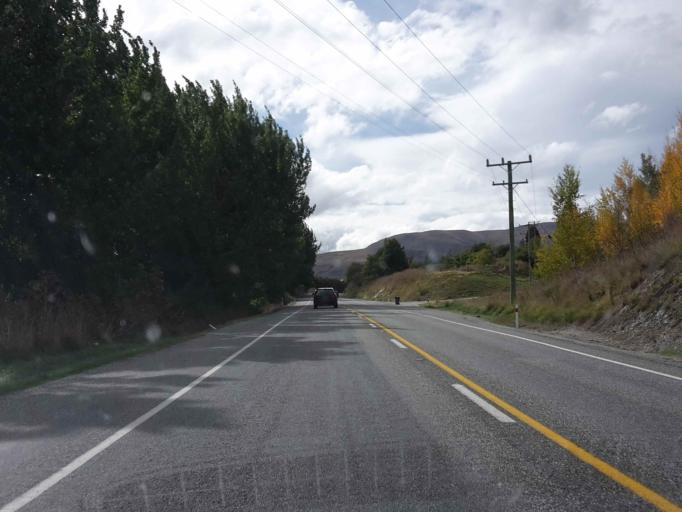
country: NZ
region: Otago
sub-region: Queenstown-Lakes District
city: Arrowtown
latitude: -44.9835
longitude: 168.8211
